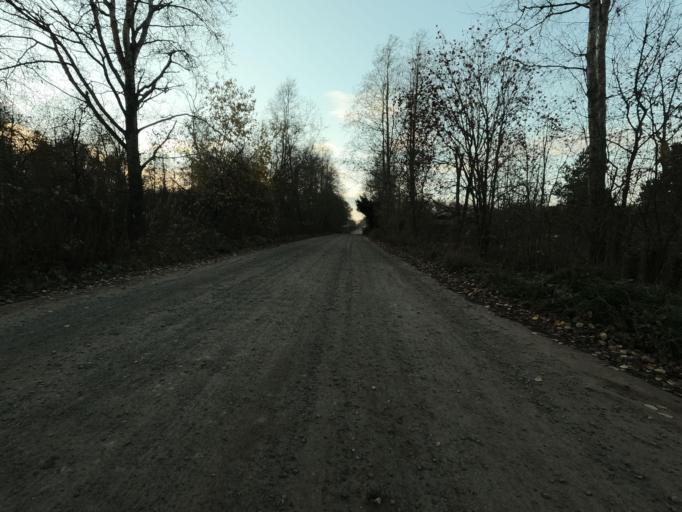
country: RU
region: Leningrad
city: Mga
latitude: 59.7639
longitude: 31.2504
